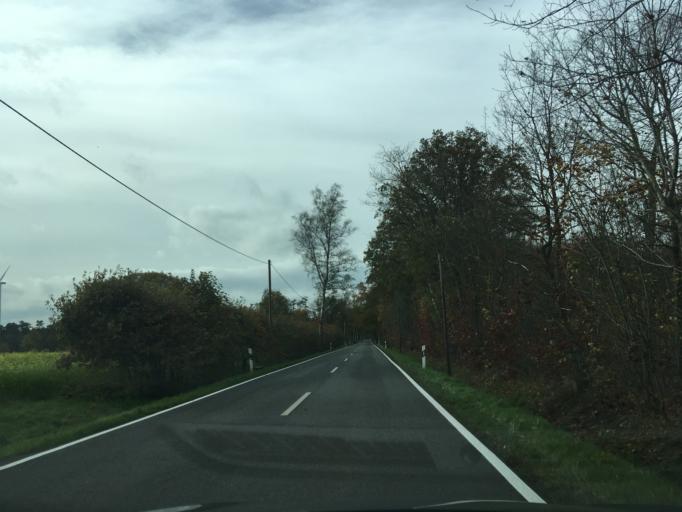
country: DE
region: North Rhine-Westphalia
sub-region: Regierungsbezirk Munster
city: Vreden
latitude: 52.0711
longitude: 6.8782
